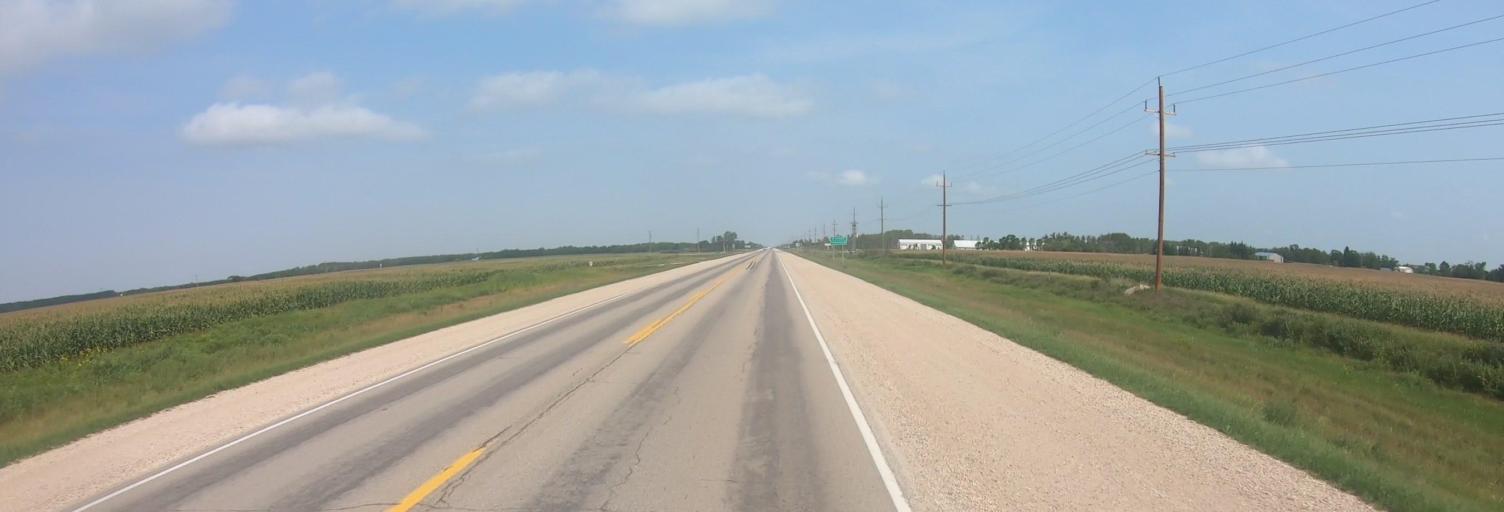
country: CA
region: Manitoba
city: Steinbach
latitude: 49.4703
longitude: -96.6911
